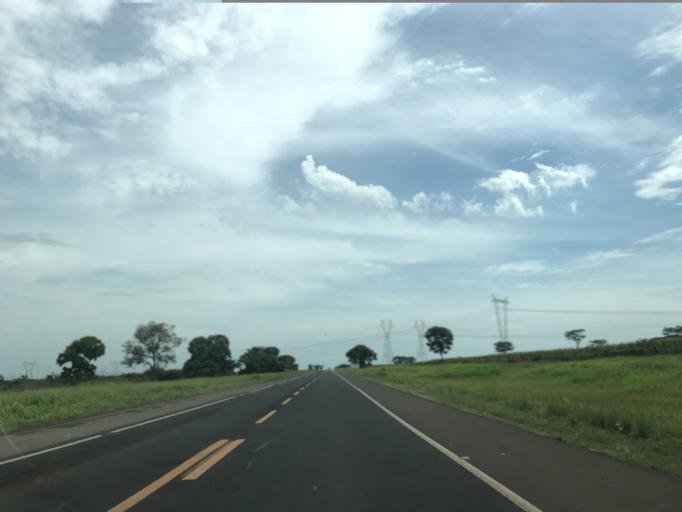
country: BR
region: Sao Paulo
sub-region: Nova Granada
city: Nova Granada
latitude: -20.3408
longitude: -49.2150
